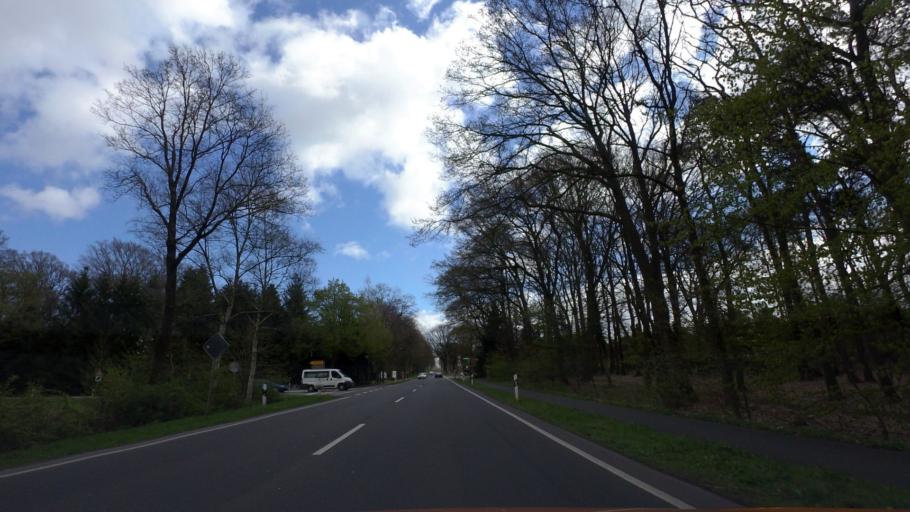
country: DE
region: Lower Saxony
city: Botersen
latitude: 53.1209
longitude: 9.3198
